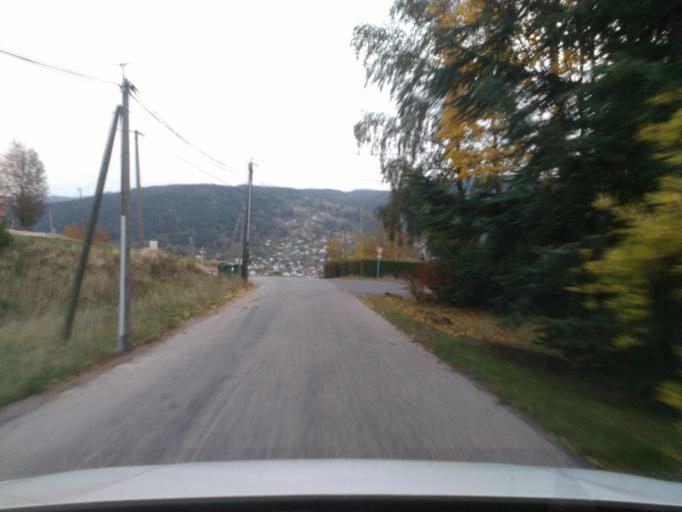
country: FR
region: Lorraine
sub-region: Departement des Vosges
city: Gerardmer
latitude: 48.0809
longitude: 6.8632
